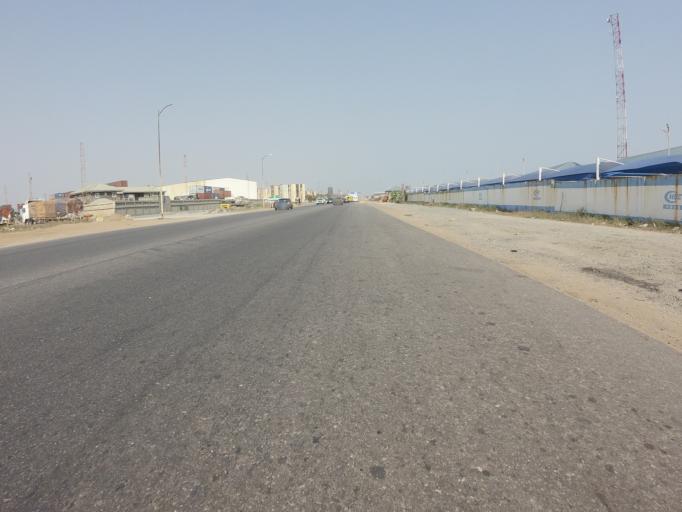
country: GH
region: Greater Accra
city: Nungua
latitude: 5.6148
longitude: -0.0272
